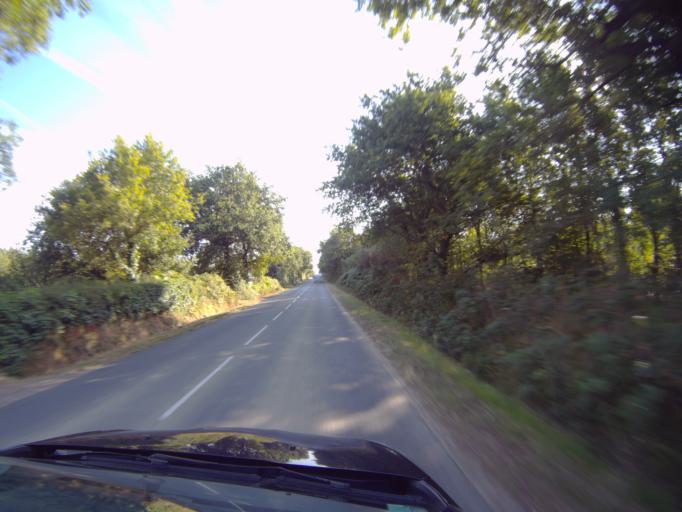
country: FR
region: Pays de la Loire
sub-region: Departement de la Vendee
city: Saint-Hilaire-de-Talmont
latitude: 46.5008
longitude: -1.5776
